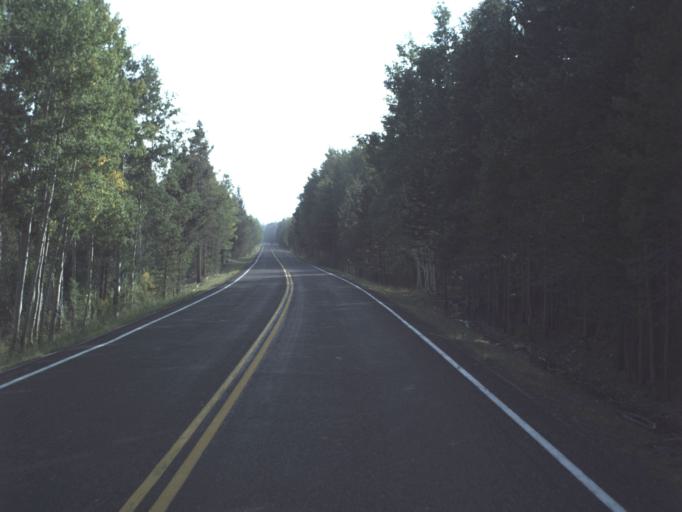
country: US
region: Utah
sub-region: Summit County
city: Oakley
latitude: 40.8223
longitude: -110.8673
